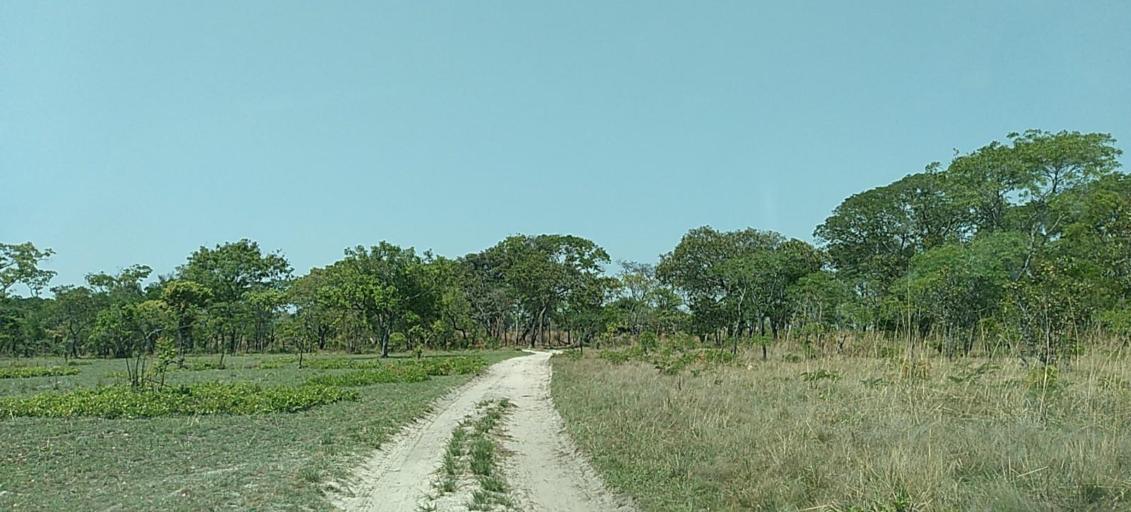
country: ZM
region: Copperbelt
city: Mpongwe
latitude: -13.8526
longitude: 28.0578
